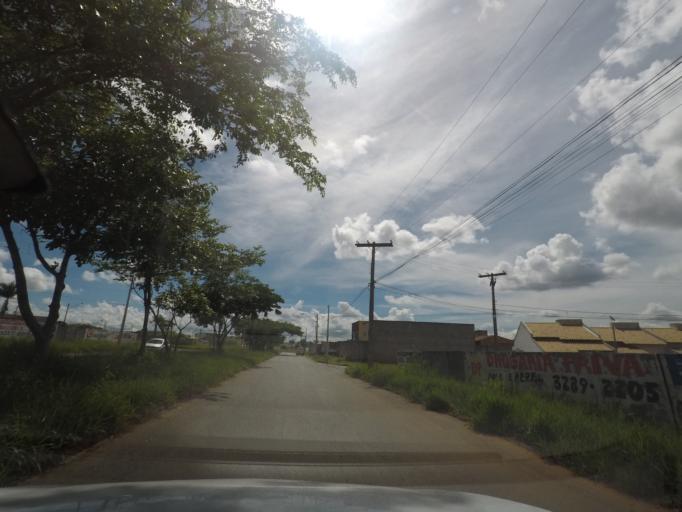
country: BR
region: Goias
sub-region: Goiania
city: Goiania
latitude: -16.7446
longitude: -49.3331
